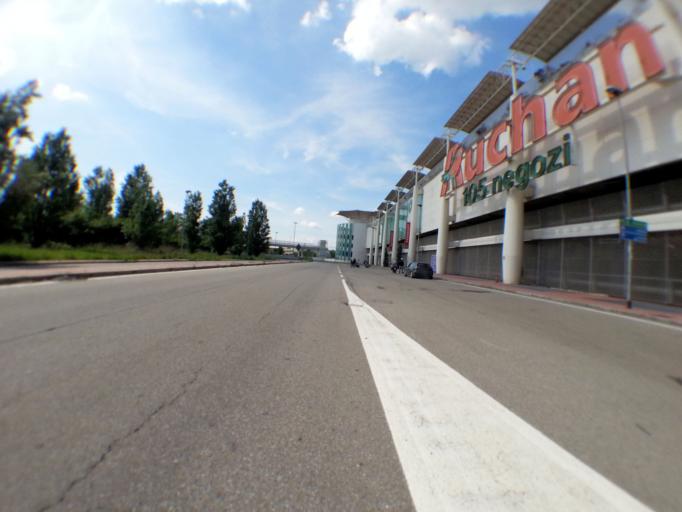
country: IT
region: Lombardy
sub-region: Citta metropolitana di Milano
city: Cinisello Balsamo
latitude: 45.5555
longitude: 9.2420
